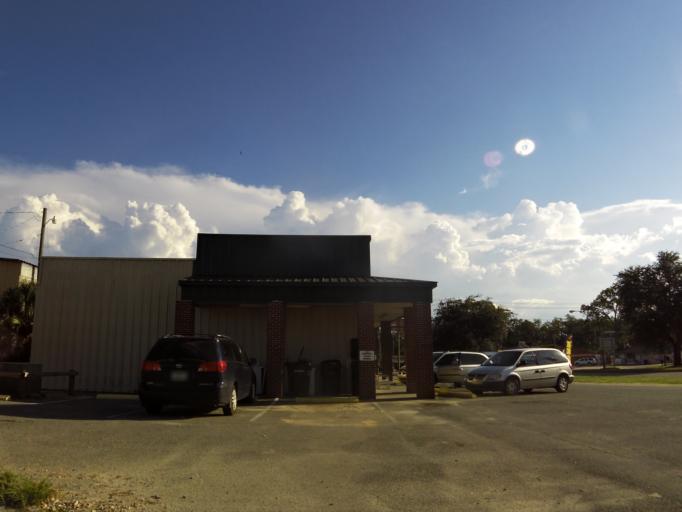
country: US
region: Georgia
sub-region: Brooks County
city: Quitman
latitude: 30.7841
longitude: -83.5597
